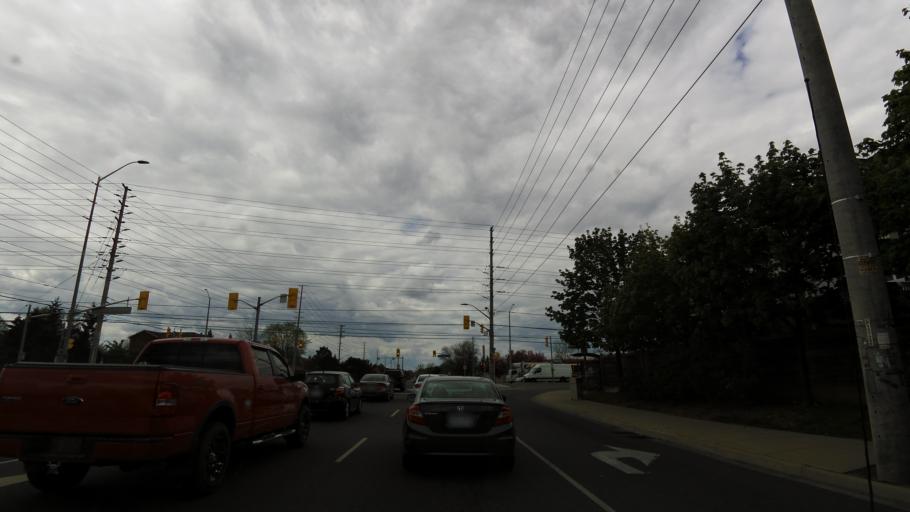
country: CA
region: Ontario
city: Mississauga
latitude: 43.5973
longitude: -79.7114
